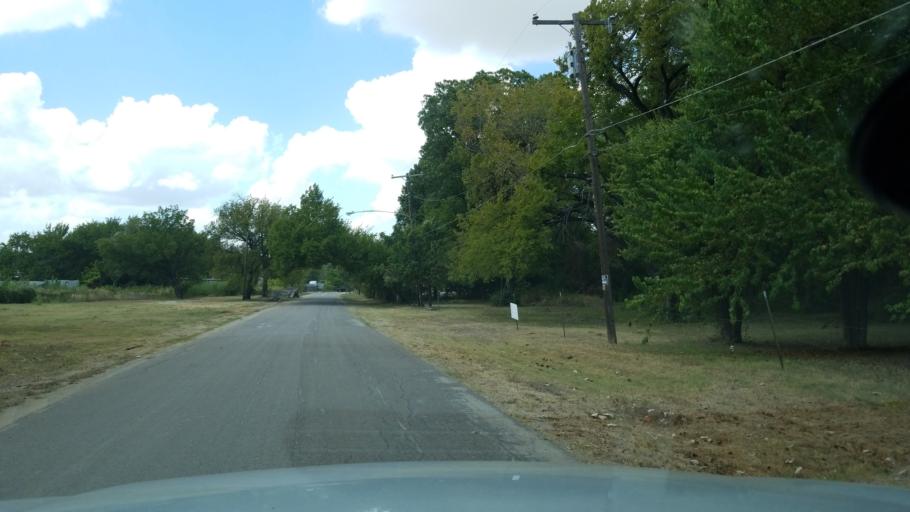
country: US
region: Texas
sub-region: Dallas County
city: Dallas
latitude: 32.7747
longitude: -96.8320
